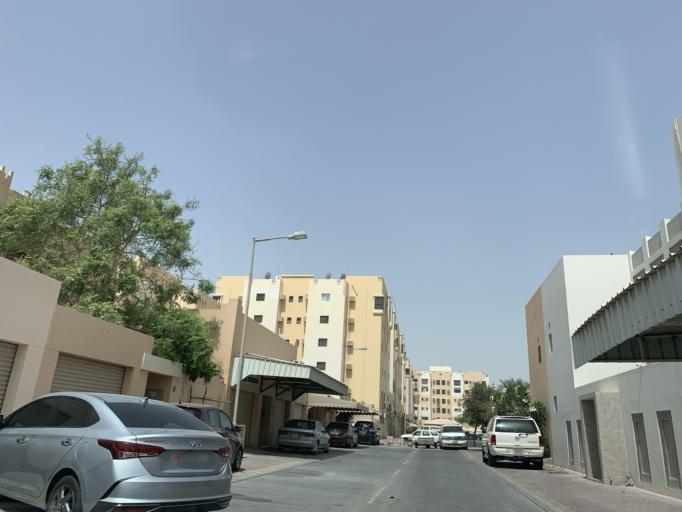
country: BH
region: Northern
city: Madinat `Isa
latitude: 26.1725
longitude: 50.5220
